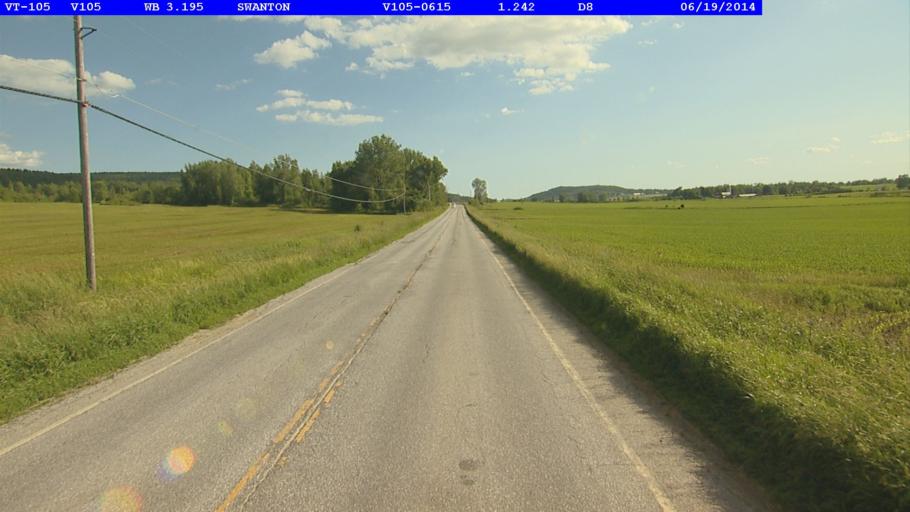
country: US
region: Vermont
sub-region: Franklin County
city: Saint Albans
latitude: 44.8508
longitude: -73.0370
